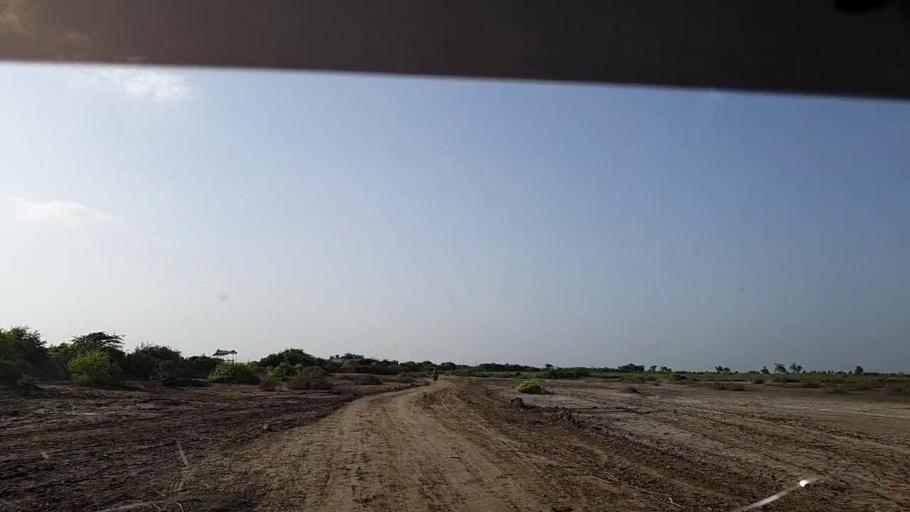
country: PK
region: Sindh
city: Badin
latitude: 24.5717
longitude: 68.8771
